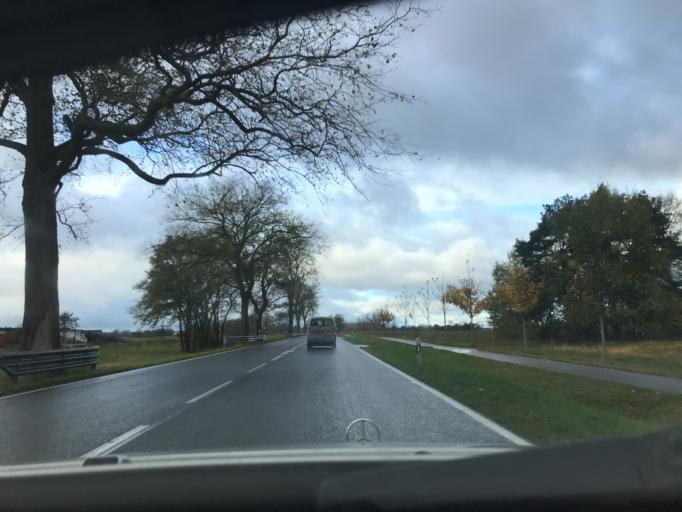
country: DE
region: Mecklenburg-Vorpommern
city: Ostseebad Zinnowitz
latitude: 54.0702
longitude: 13.8814
